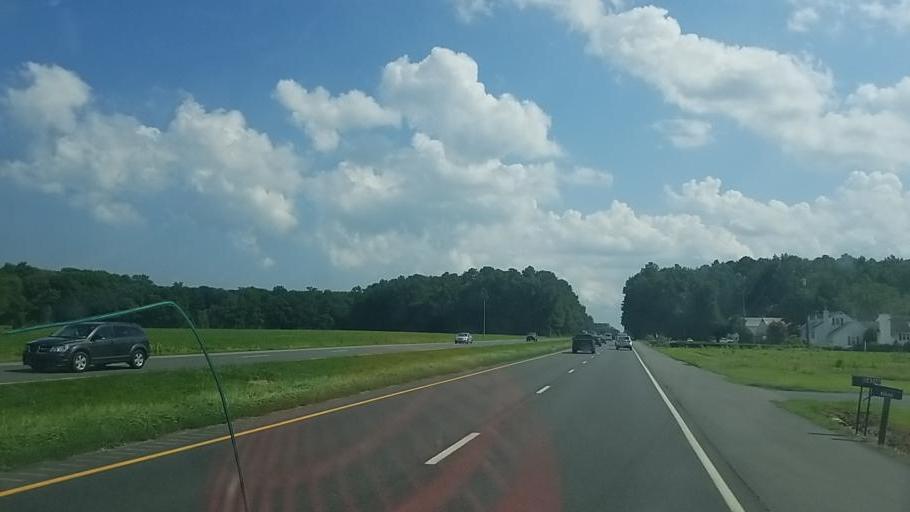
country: US
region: Delaware
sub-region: Sussex County
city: Selbyville
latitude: 38.5087
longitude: -75.2381
